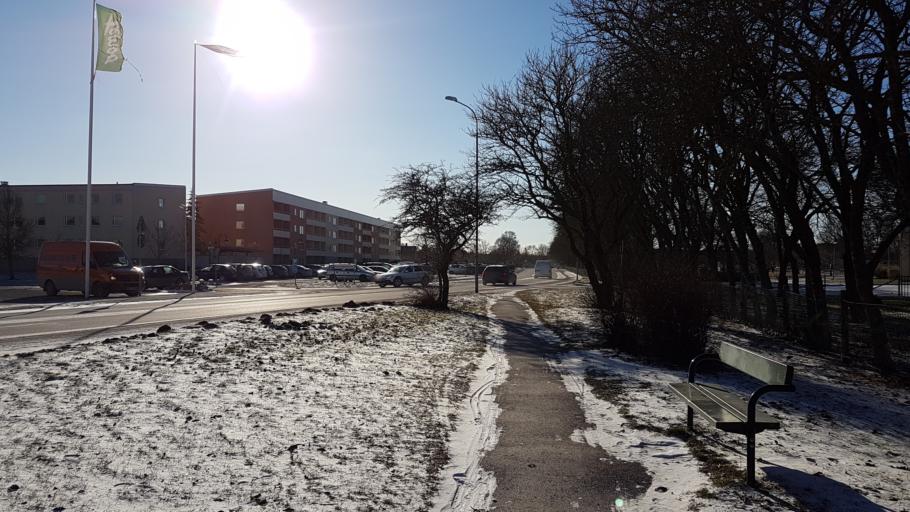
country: SE
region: Gotland
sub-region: Gotland
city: Visby
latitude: 57.6395
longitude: 18.3120
